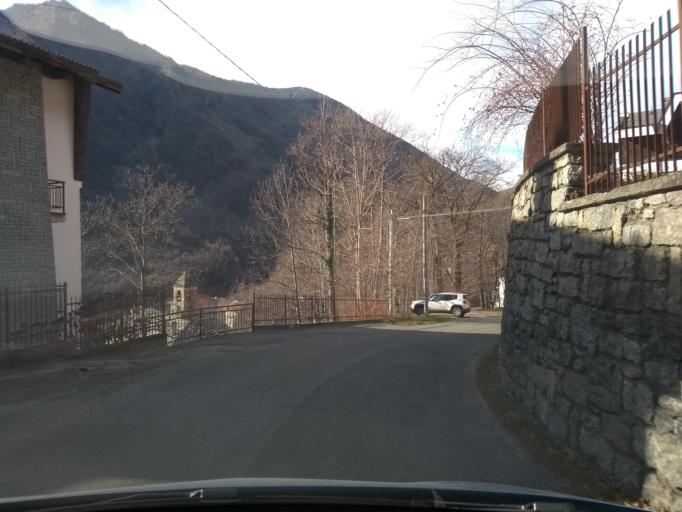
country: IT
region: Piedmont
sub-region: Provincia di Torino
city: Cantoira
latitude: 45.3443
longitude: 7.3810
